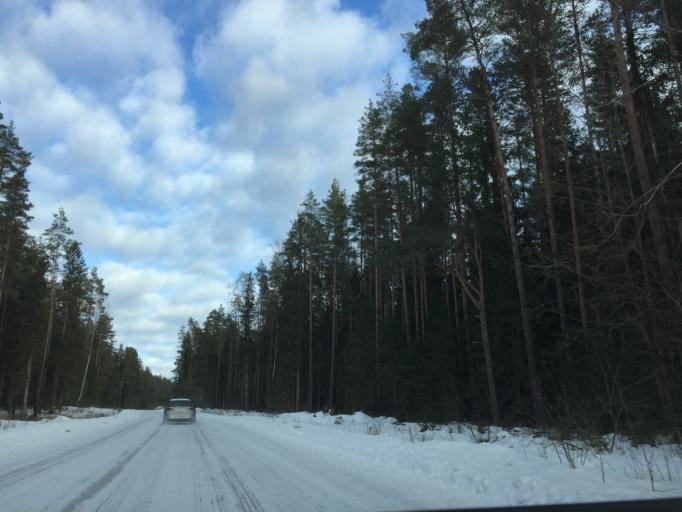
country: LV
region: Ogre
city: Jumprava
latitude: 56.5543
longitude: 24.8993
